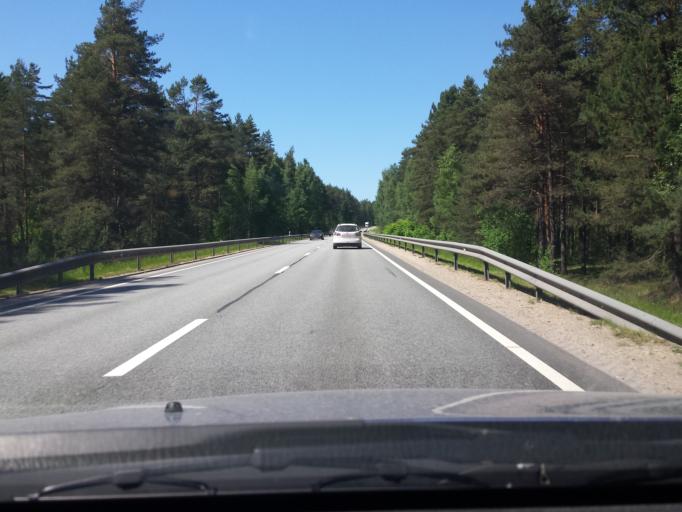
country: LV
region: Riga
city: Bergi
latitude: 56.9804
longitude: 24.3289
